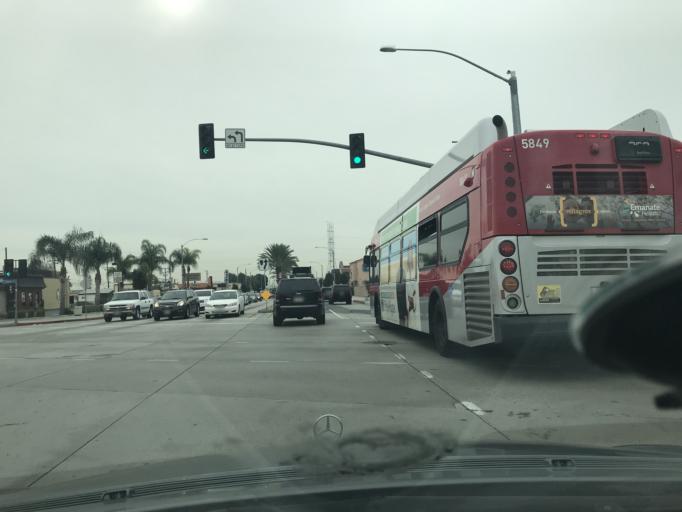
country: US
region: California
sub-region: Los Angeles County
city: Cudahy
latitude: 33.9520
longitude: -118.1833
